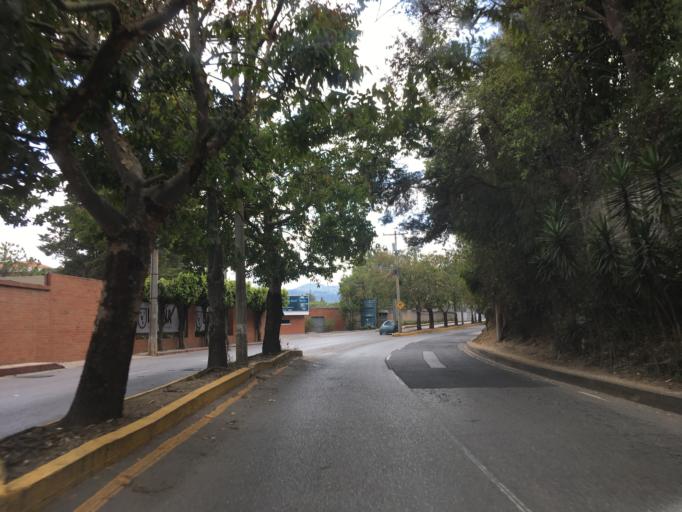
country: GT
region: Guatemala
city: Guatemala City
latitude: 14.6164
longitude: -90.4722
